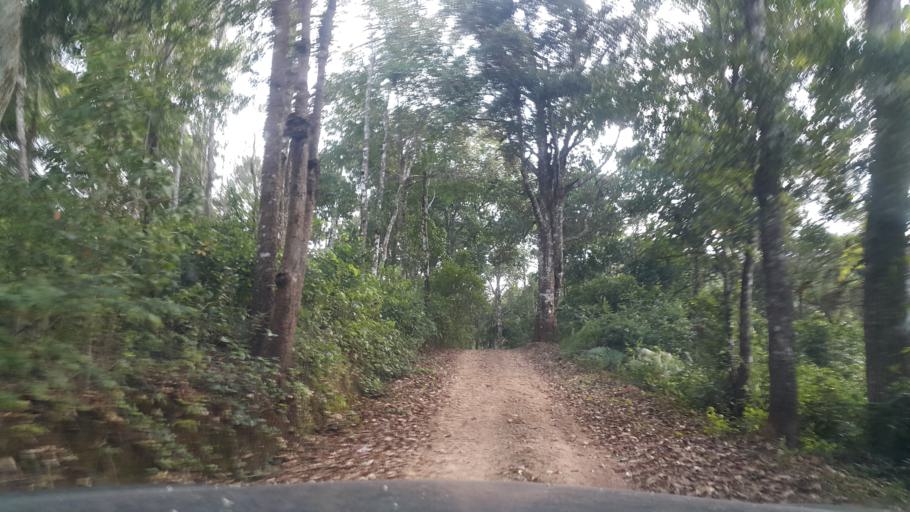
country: TH
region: Chiang Mai
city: Samoeng
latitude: 19.0358
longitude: 98.6533
